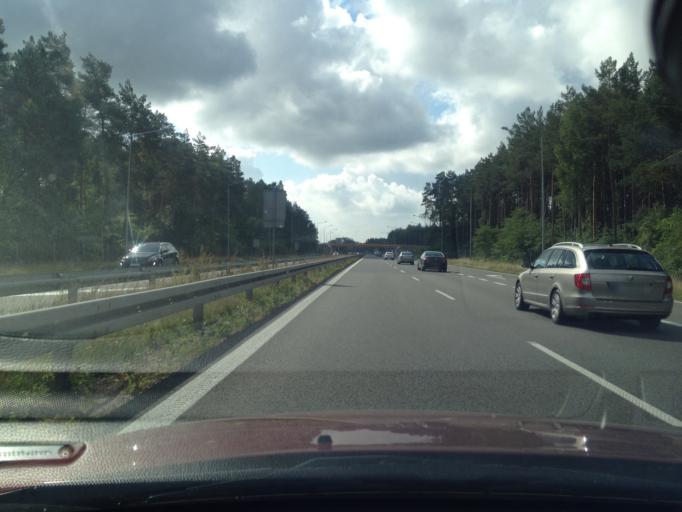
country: PL
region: West Pomeranian Voivodeship
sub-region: Powiat goleniowski
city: Goleniow
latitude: 53.6293
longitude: 14.8184
